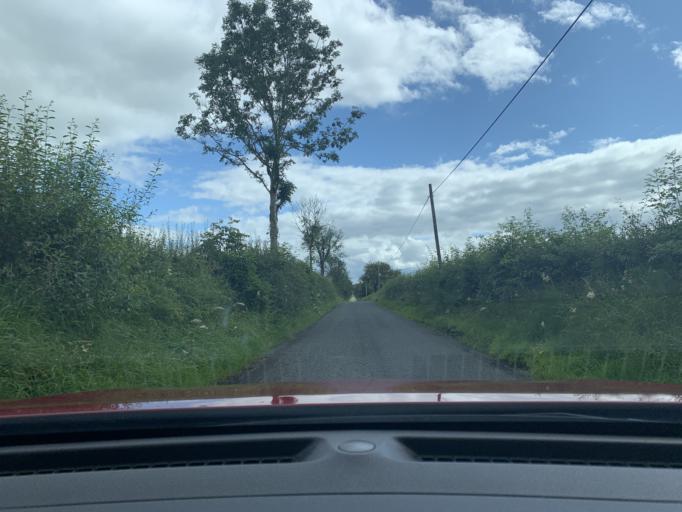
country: GB
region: Northern Ireland
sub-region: Fermanagh District
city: Enniskillen
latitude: 54.2764
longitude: -7.8181
